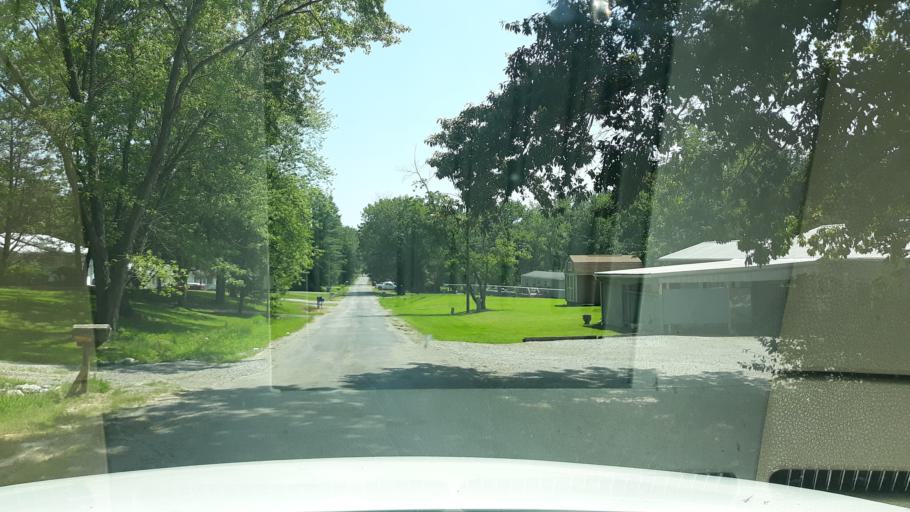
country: US
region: Illinois
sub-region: Saline County
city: Harrisburg
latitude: 37.8475
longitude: -88.6100
